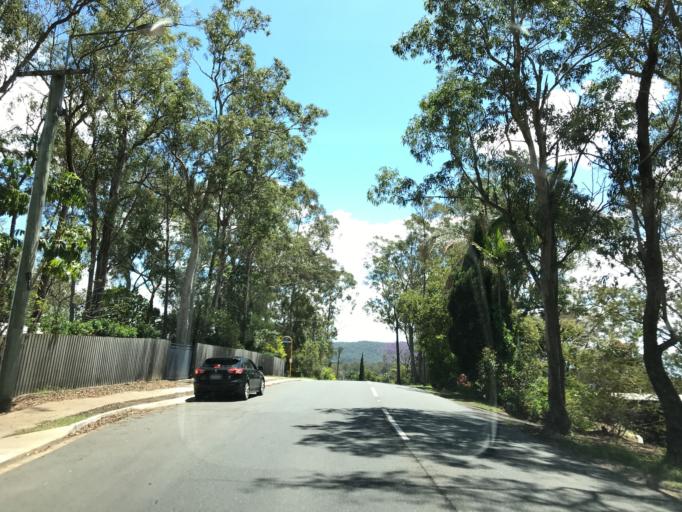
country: AU
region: Queensland
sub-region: Brisbane
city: Seventeen Mile Rocks
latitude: -27.5228
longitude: 152.9567
